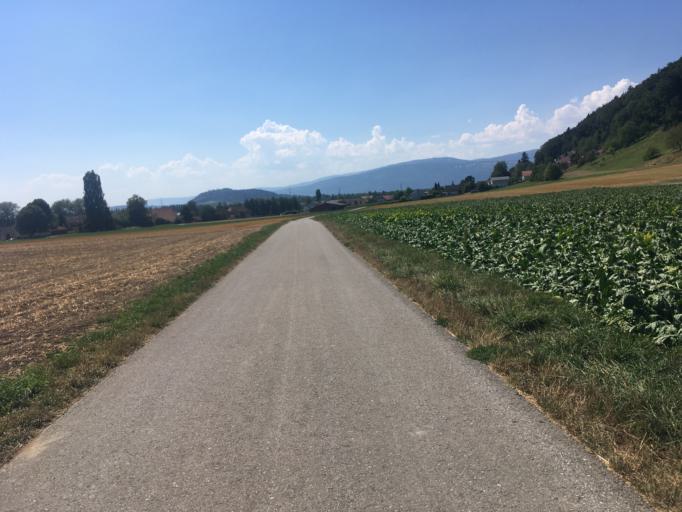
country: CH
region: Bern
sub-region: Biel/Bienne District
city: Meinisberg
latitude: 47.1188
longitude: 7.3539
